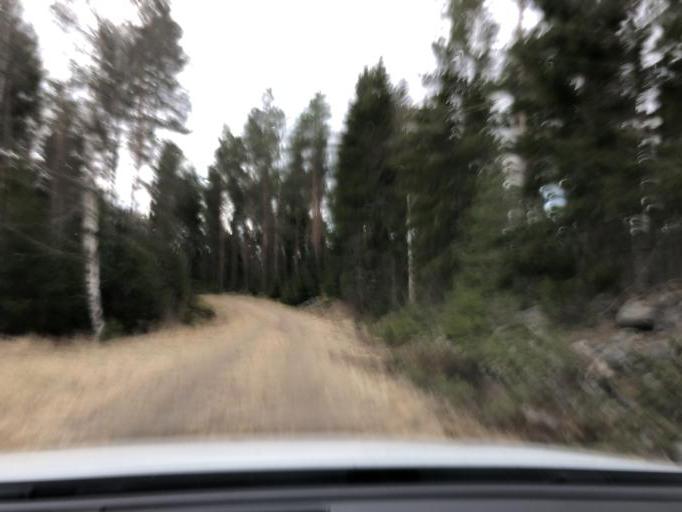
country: SE
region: Gaevleborg
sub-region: Gavle Kommun
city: Hedesunda
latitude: 60.3389
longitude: 17.0640
